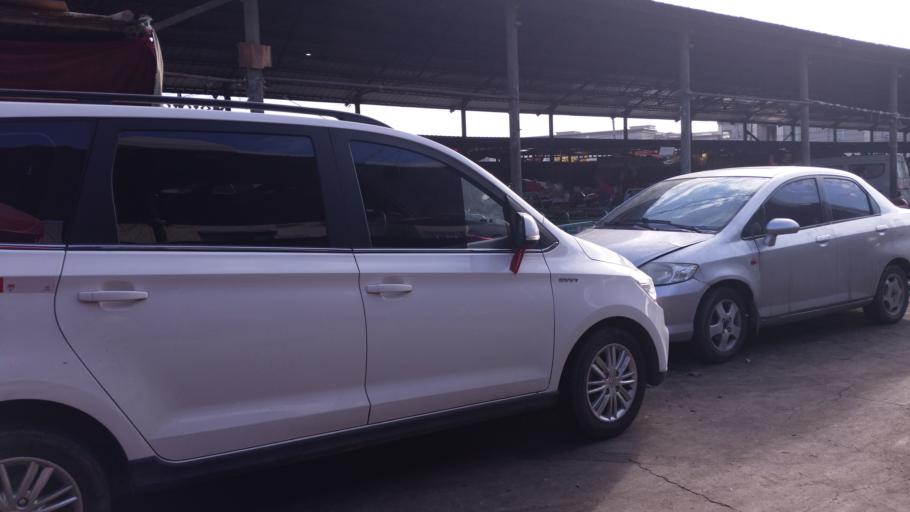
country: CN
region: Xinjiang Uygur Zizhiqu
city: Laochenglu
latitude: 42.9404
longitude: 89.1733
